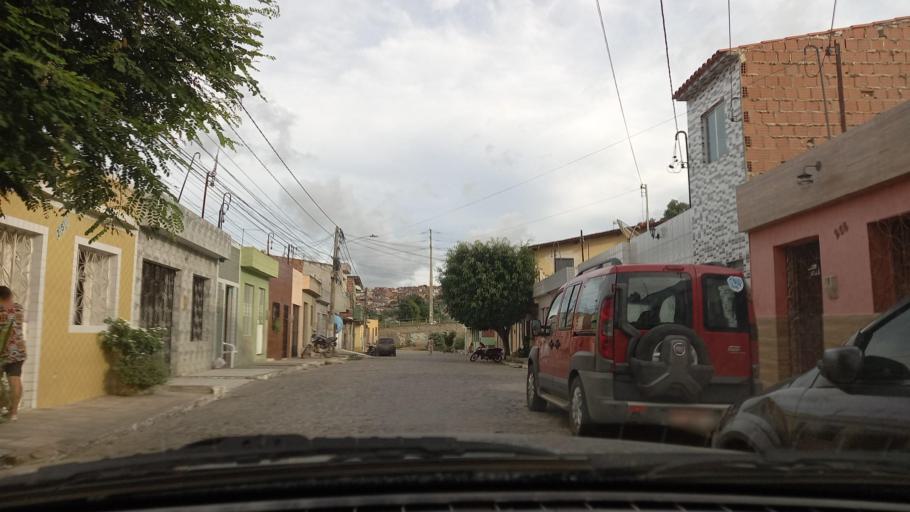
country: BR
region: Pernambuco
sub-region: Gravata
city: Gravata
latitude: -8.2042
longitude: -35.5649
